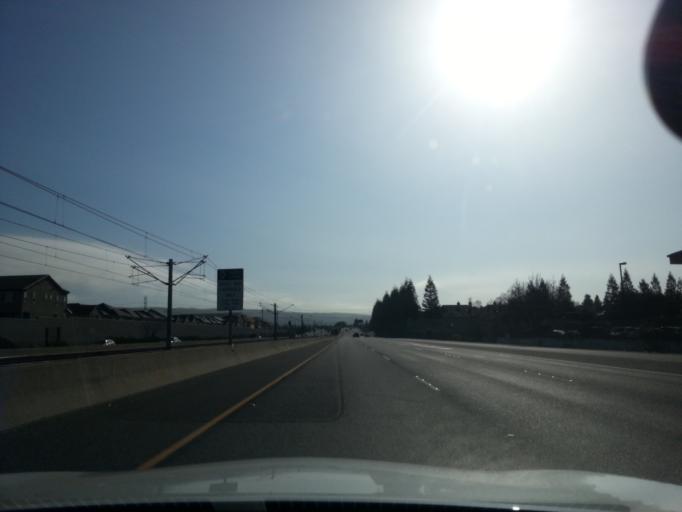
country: US
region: California
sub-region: Santa Clara County
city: Seven Trees
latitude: 37.2415
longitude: -121.7991
